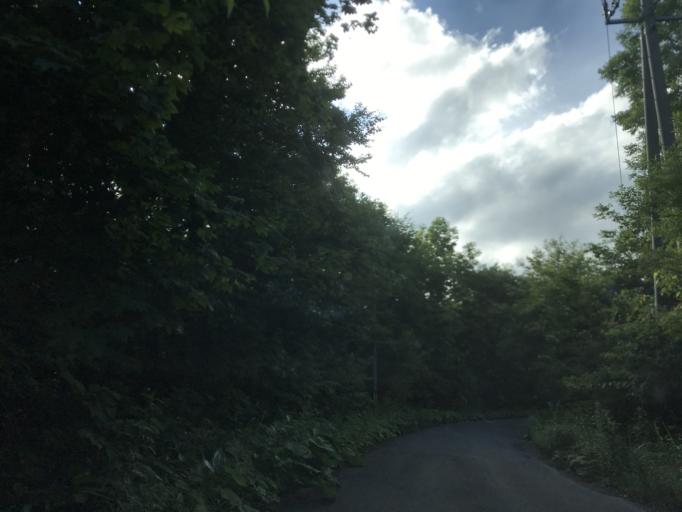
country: JP
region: Iwate
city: Ichinoseki
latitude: 38.9241
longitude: 140.8350
